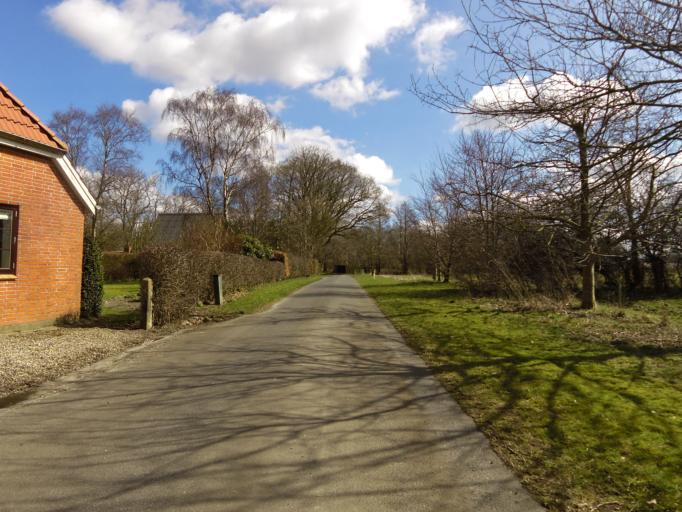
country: DK
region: South Denmark
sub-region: Tonder Kommune
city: Toftlund
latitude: 55.1536
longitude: 9.0355
